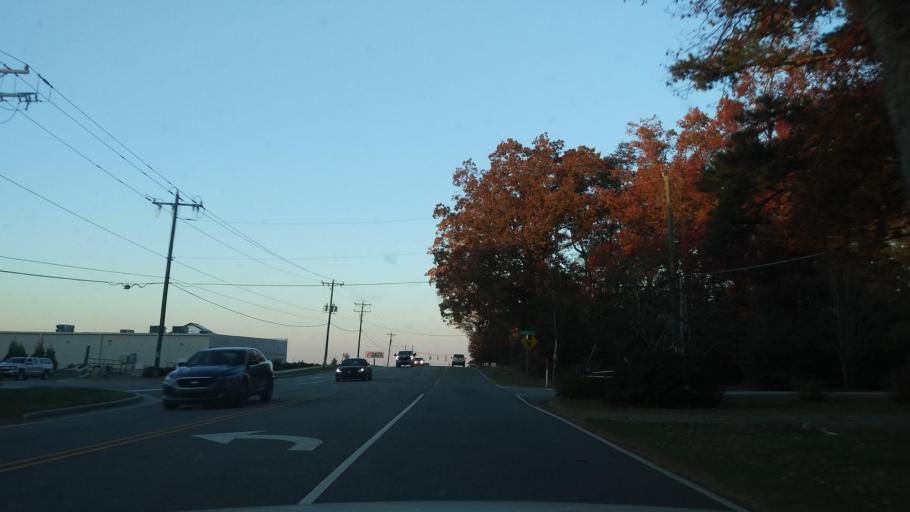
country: US
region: North Carolina
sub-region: Guilford County
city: Pleasant Garden
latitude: 35.9948
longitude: -79.7930
